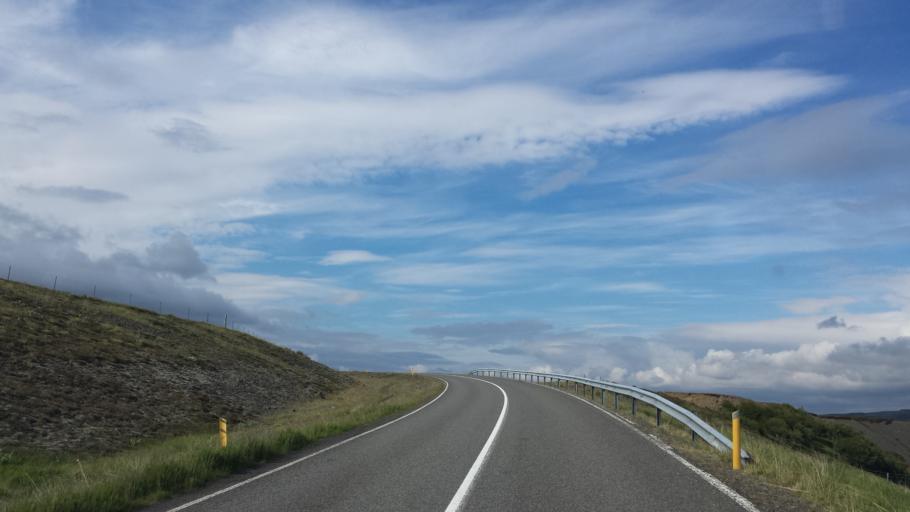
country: IS
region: South
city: Vestmannaeyjar
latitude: 64.2636
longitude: -20.2242
